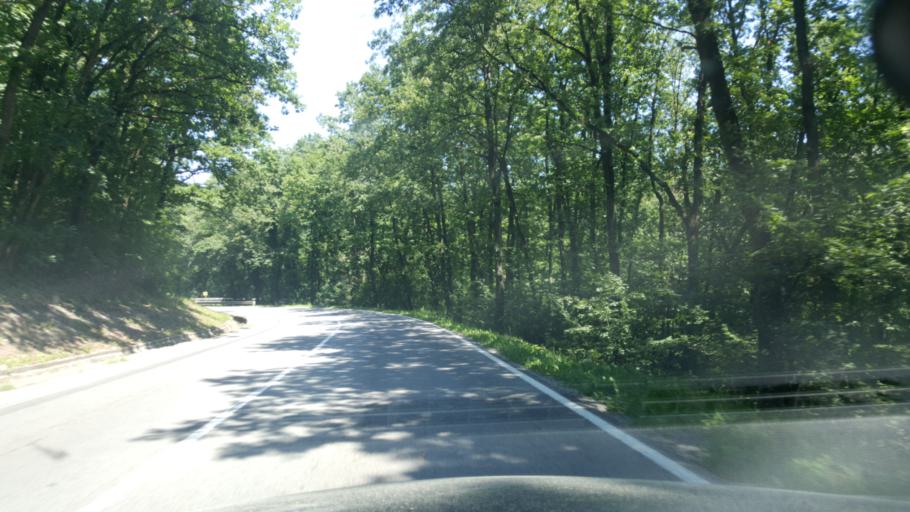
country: RS
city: Rusanj
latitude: 44.6837
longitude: 20.5136
